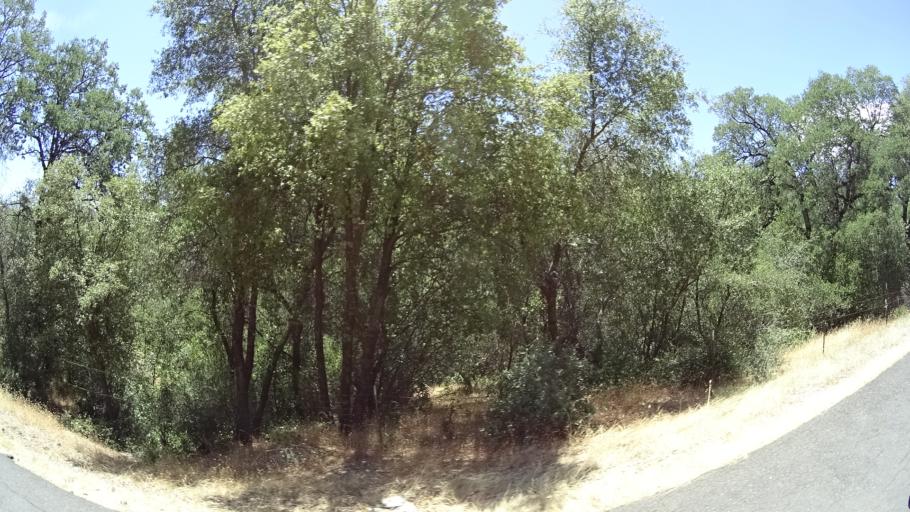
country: US
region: California
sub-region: Calaveras County
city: Forest Meadows
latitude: 38.2087
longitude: -120.4598
